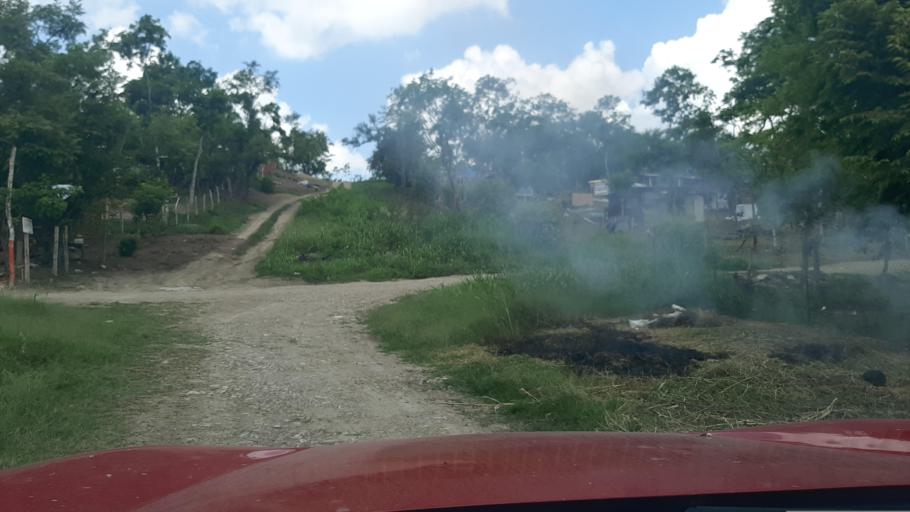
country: MX
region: Veracruz
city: Coatzintla
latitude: 20.5042
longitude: -97.4596
